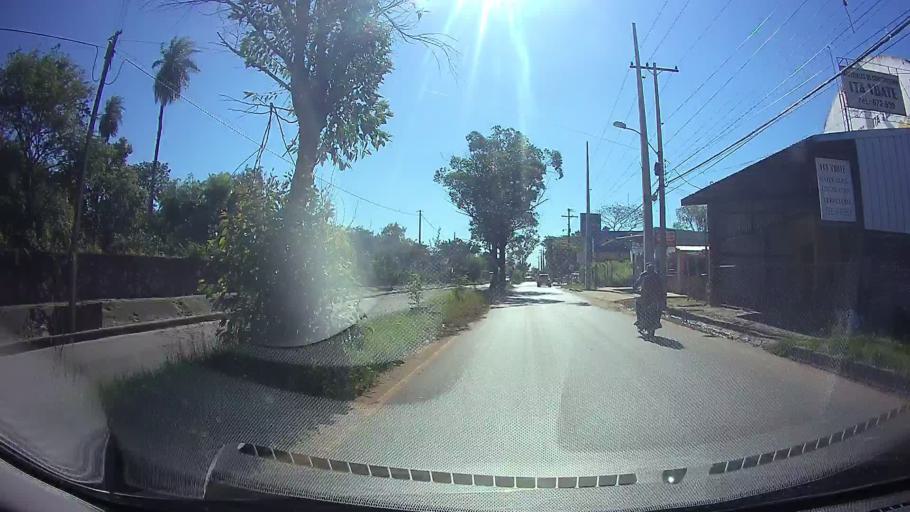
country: PY
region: Central
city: Fernando de la Mora
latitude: -25.2963
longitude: -57.5215
